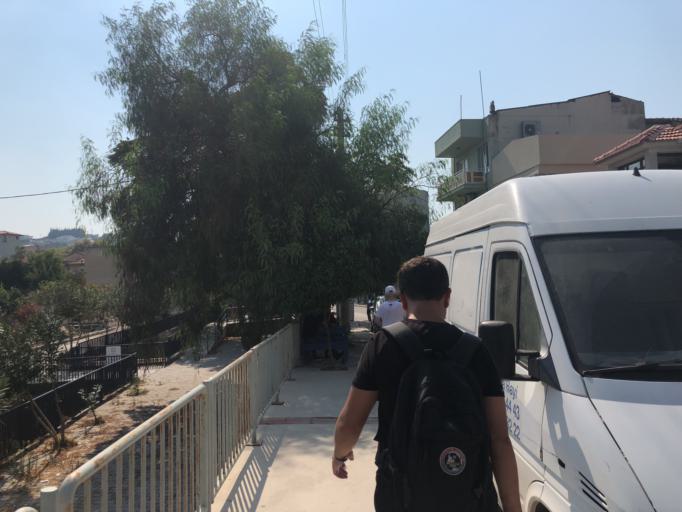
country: TR
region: Izmir
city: Urla
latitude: 38.3230
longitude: 26.7651
